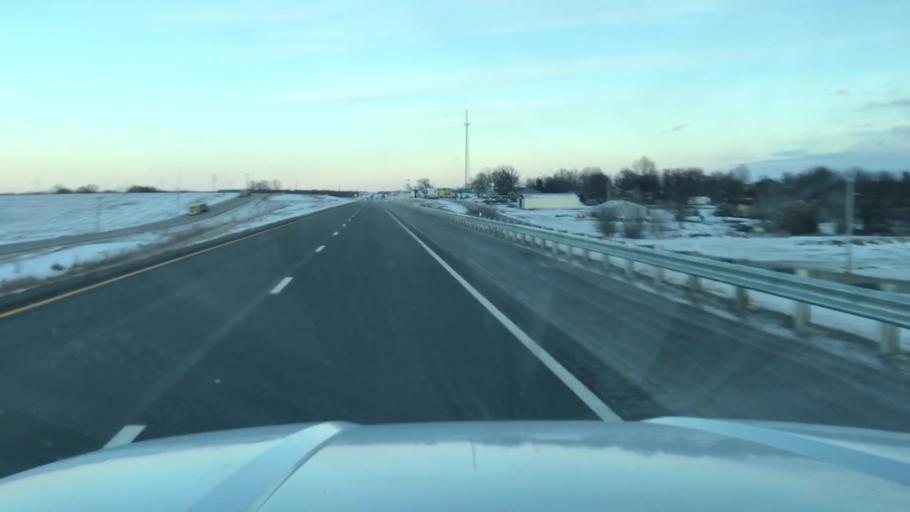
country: US
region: Missouri
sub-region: Clinton County
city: Gower
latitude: 39.7620
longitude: -94.5055
